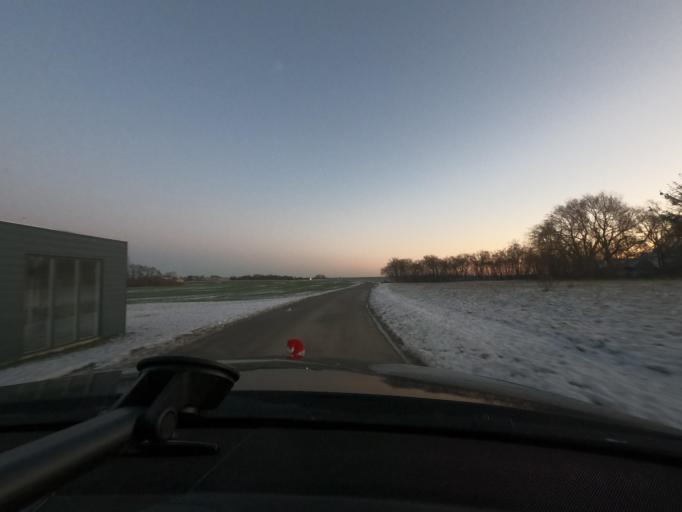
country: DK
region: South Denmark
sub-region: Sonderborg Kommune
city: Horuphav
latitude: 54.8692
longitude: 9.8966
